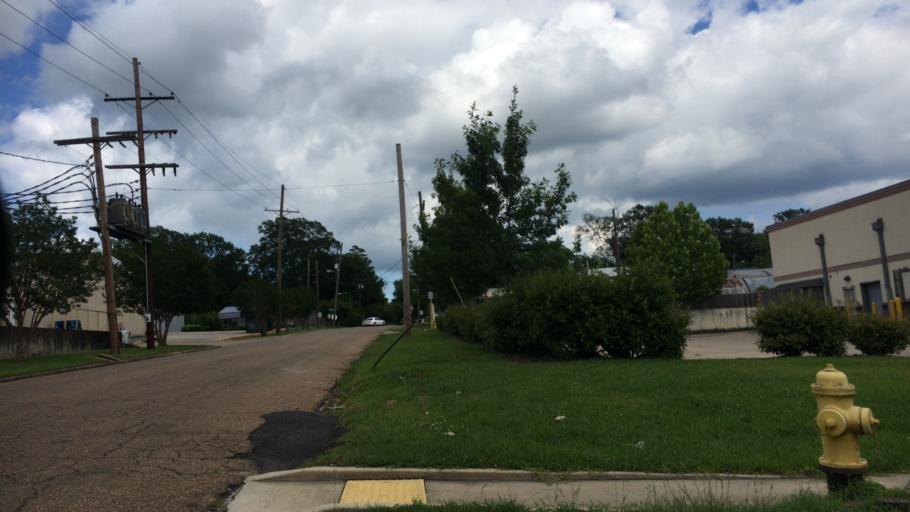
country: US
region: Louisiana
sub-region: Lincoln Parish
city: Ruston
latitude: 32.5248
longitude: -92.6395
